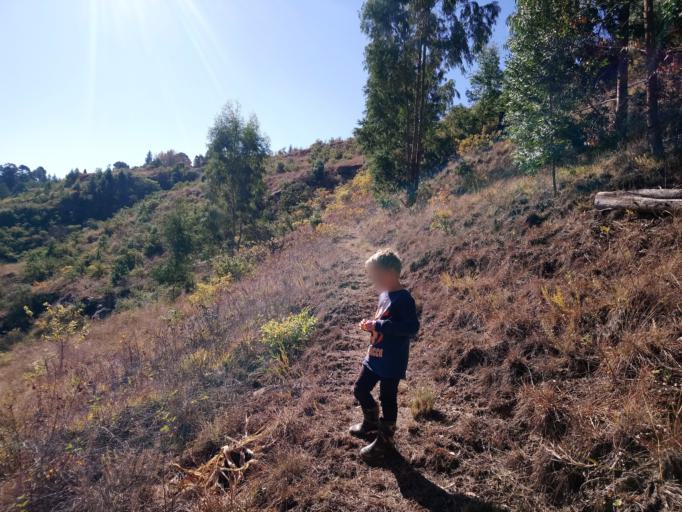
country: ZA
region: KwaZulu-Natal
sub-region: uMgungundlovu District Municipality
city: Mooirivier
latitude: -29.3334
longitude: 29.9182
